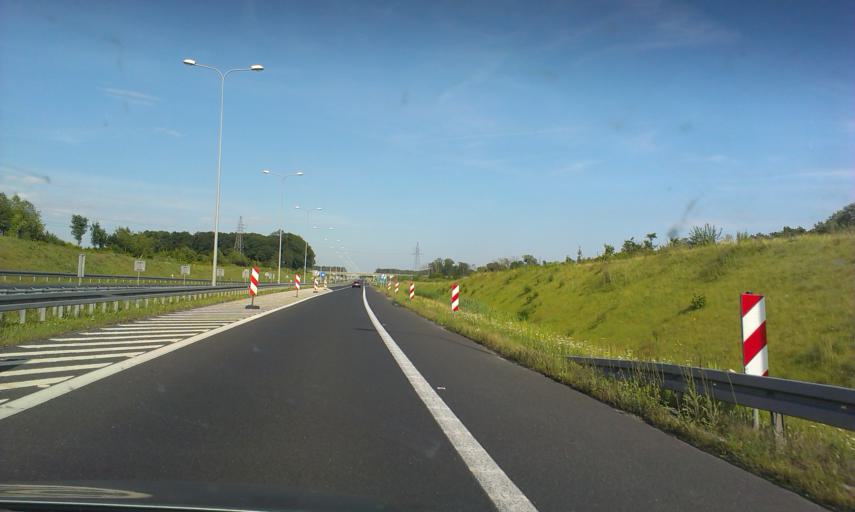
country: PL
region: Greater Poland Voivodeship
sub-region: Powiat pilski
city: Wyrzysk
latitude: 53.1630
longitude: 17.2141
